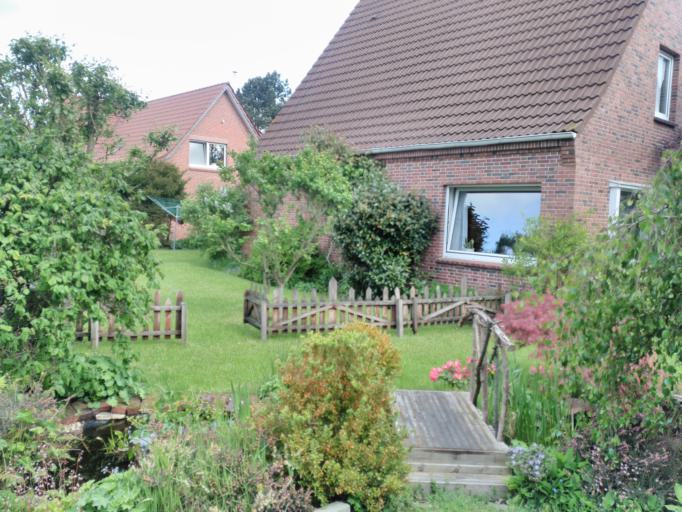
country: DE
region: Lower Saxony
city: Norden
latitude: 53.5869
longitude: 7.2107
